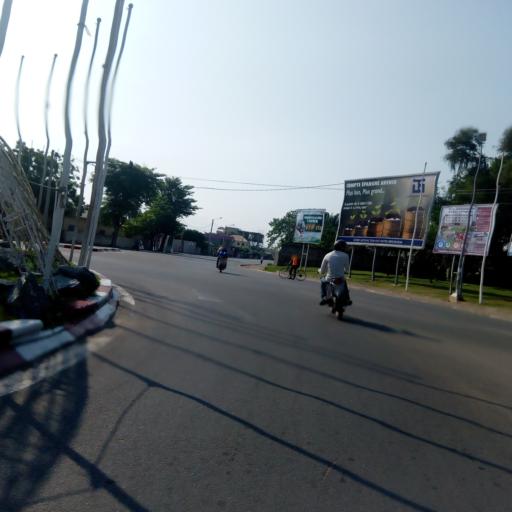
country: TG
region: Maritime
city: Lome
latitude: 6.1369
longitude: 1.2221
